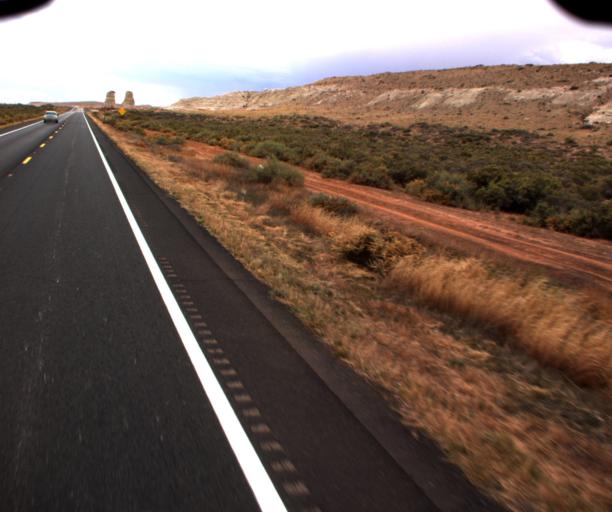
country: US
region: Arizona
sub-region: Coconino County
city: Kaibito
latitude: 36.3362
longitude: -110.9208
